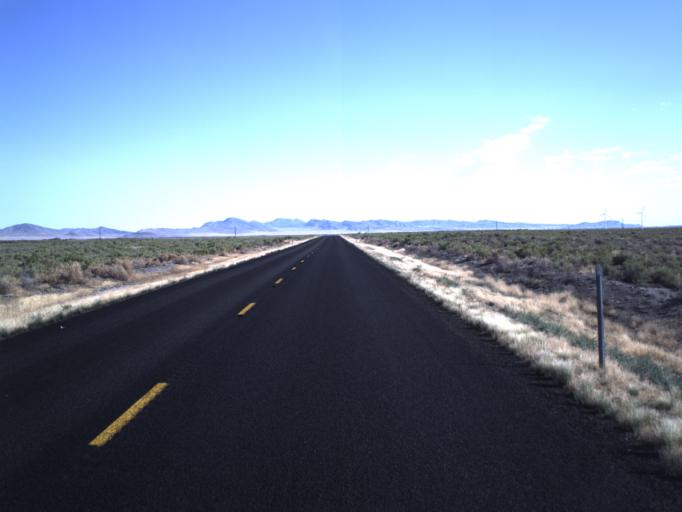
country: US
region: Utah
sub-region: Beaver County
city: Milford
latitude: 38.5509
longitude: -112.9912
